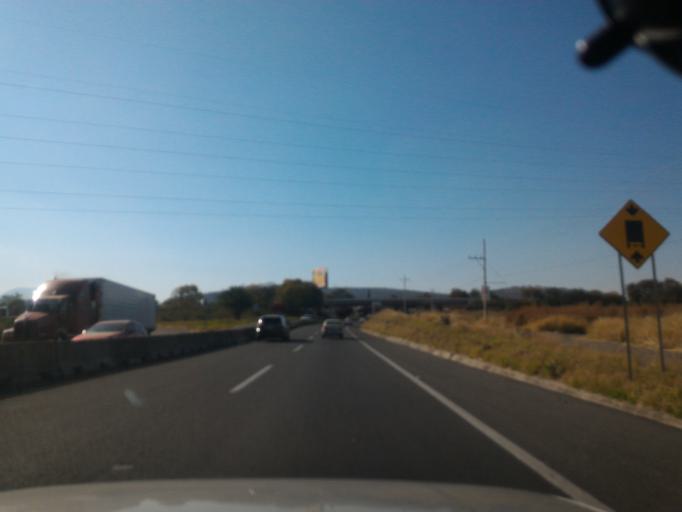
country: MX
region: Jalisco
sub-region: Ixtlahuacan de los Membrillos
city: Los Cedros
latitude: 20.4147
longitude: -103.2313
